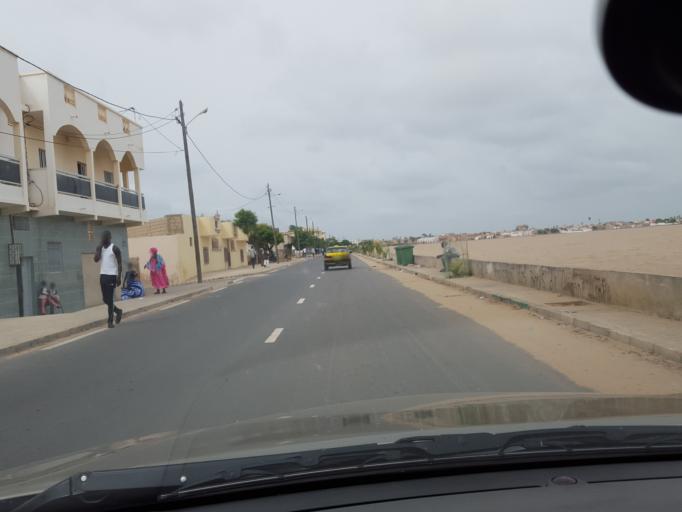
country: SN
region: Saint-Louis
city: Saint-Louis
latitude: 16.0316
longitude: -16.4920
